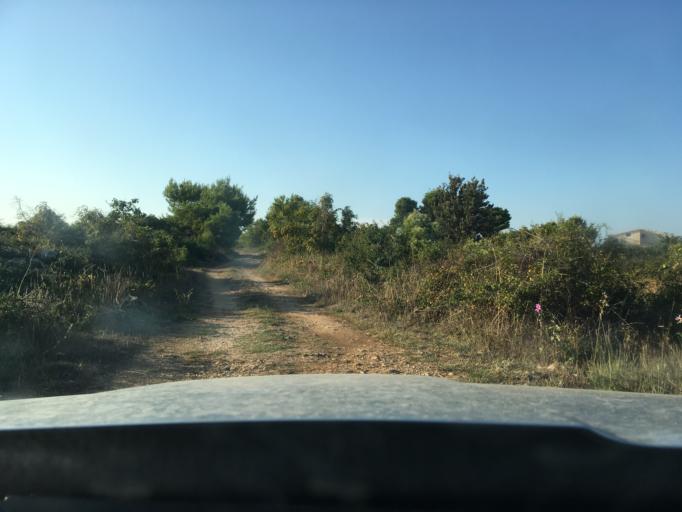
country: HR
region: Zadarska
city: Vir
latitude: 44.2971
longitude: 15.0752
